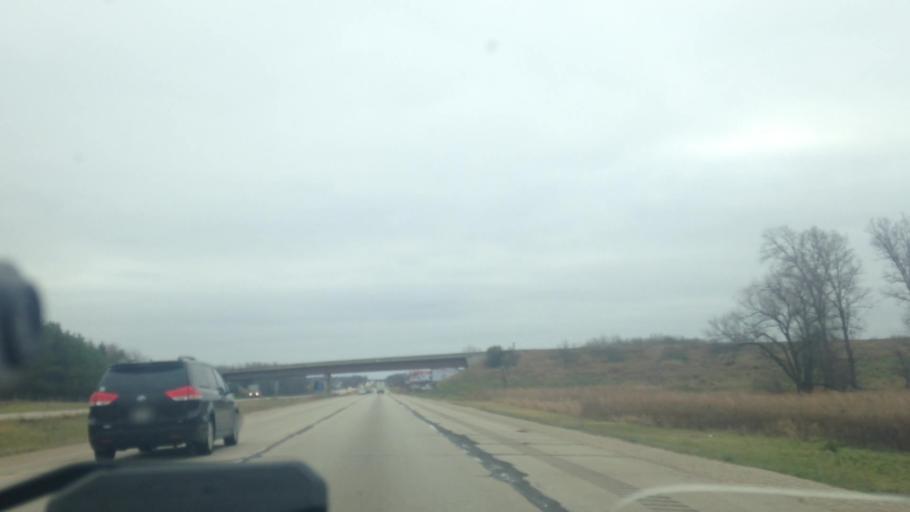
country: US
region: Wisconsin
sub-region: Washington County
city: Slinger
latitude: 43.3116
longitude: -88.2333
